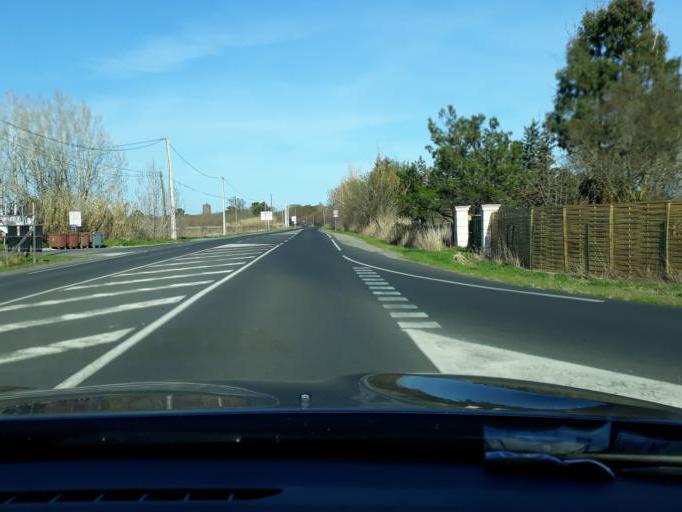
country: FR
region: Languedoc-Roussillon
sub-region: Departement de l'Herault
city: Agde
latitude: 43.3049
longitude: 3.4571
